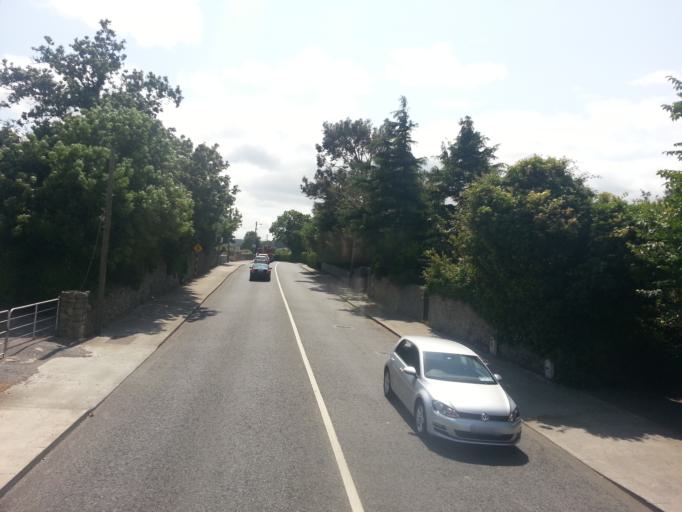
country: IE
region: Leinster
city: Foxrock
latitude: 53.2391
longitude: -6.1962
